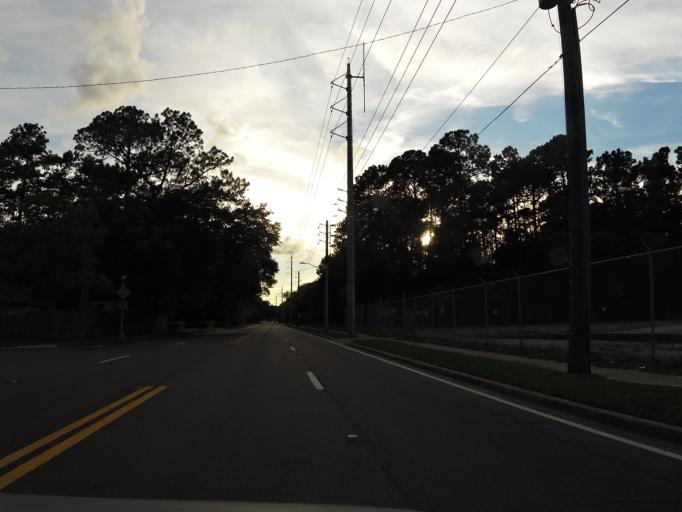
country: US
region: Florida
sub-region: Duval County
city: Jacksonville
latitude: 30.4043
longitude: -81.7145
